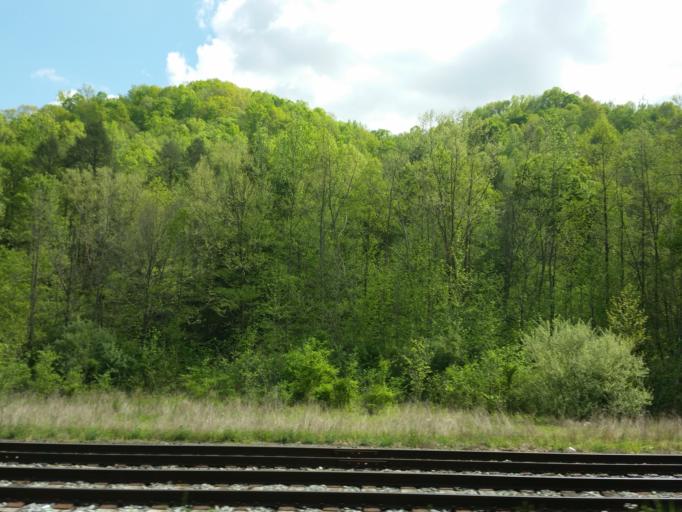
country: US
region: Kentucky
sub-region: Bell County
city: Middlesboro
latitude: 36.6142
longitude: -83.7713
